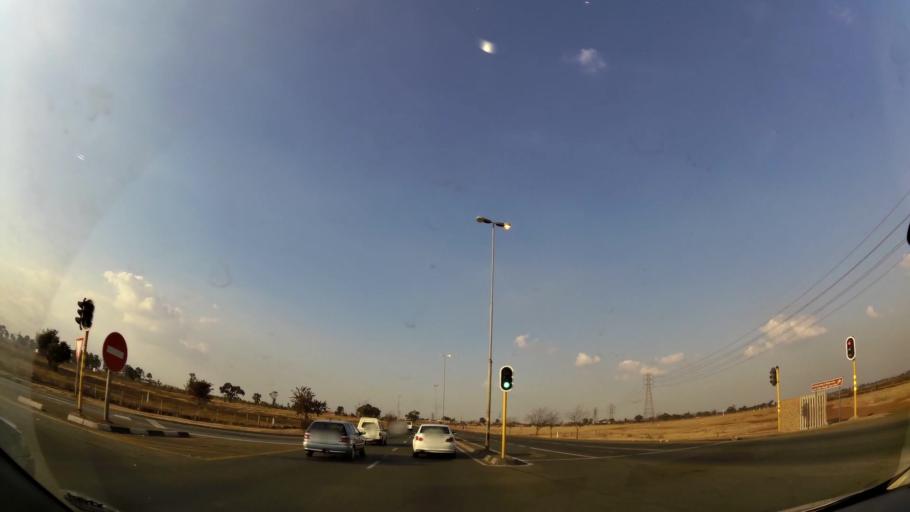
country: ZA
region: Gauteng
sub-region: Ekurhuleni Metropolitan Municipality
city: Germiston
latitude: -26.3404
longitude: 28.2223
